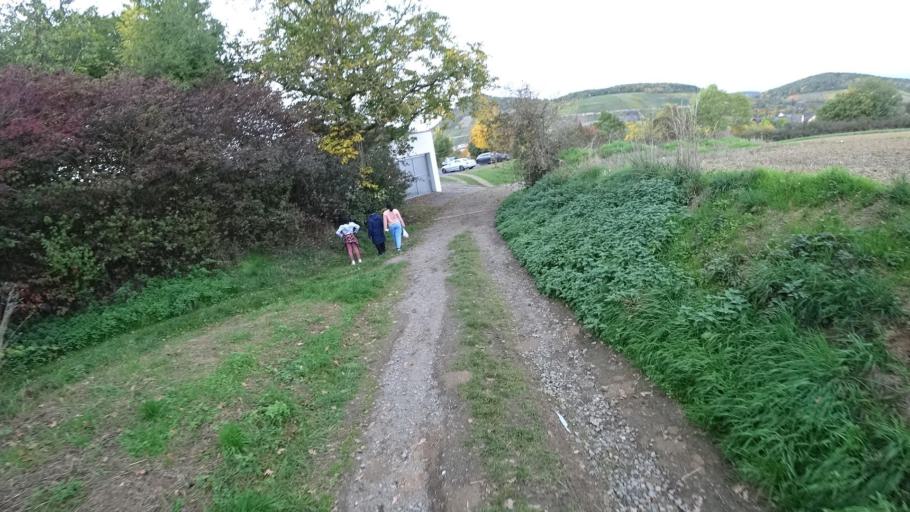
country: DE
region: Rheinland-Pfalz
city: Konigsfeld
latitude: 50.5399
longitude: 7.1825
